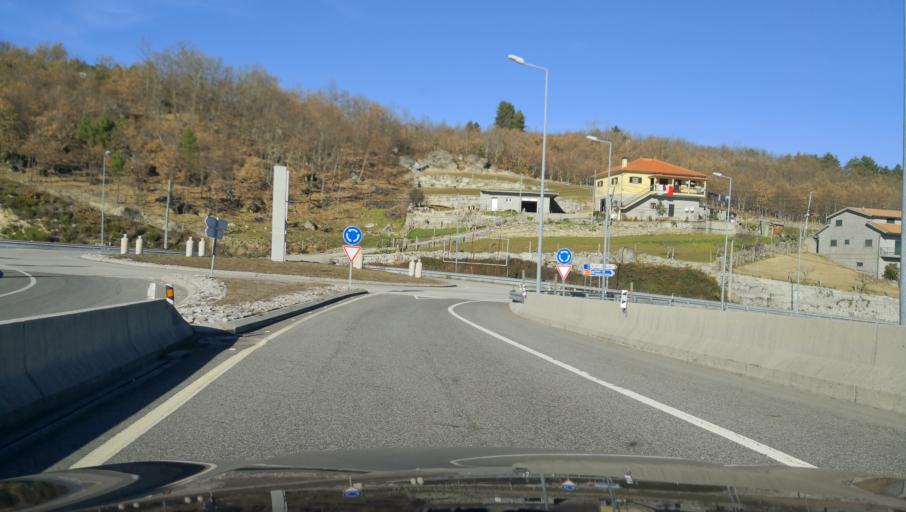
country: PT
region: Vila Real
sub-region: Vila Pouca de Aguiar
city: Vila Pouca de Aguiar
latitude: 41.4902
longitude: -7.6591
